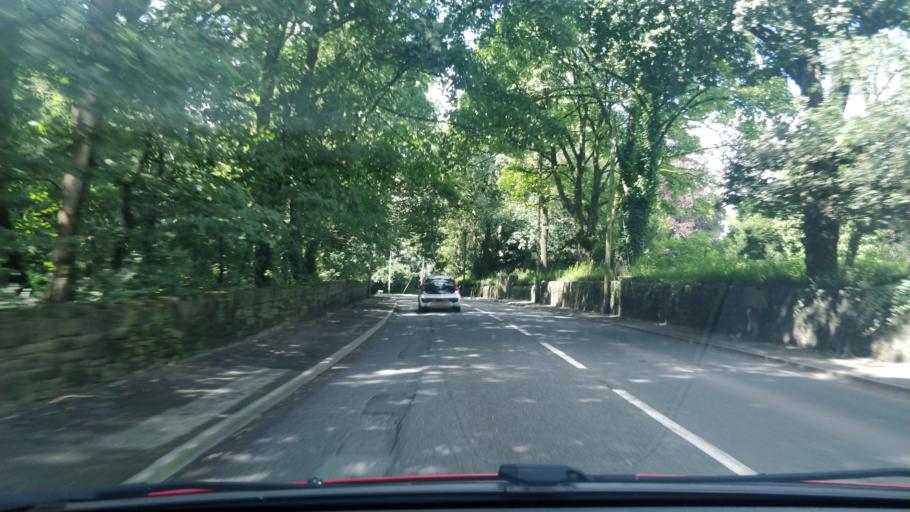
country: GB
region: England
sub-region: Borough of Wigan
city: Shevington
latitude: 53.5921
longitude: -2.7003
